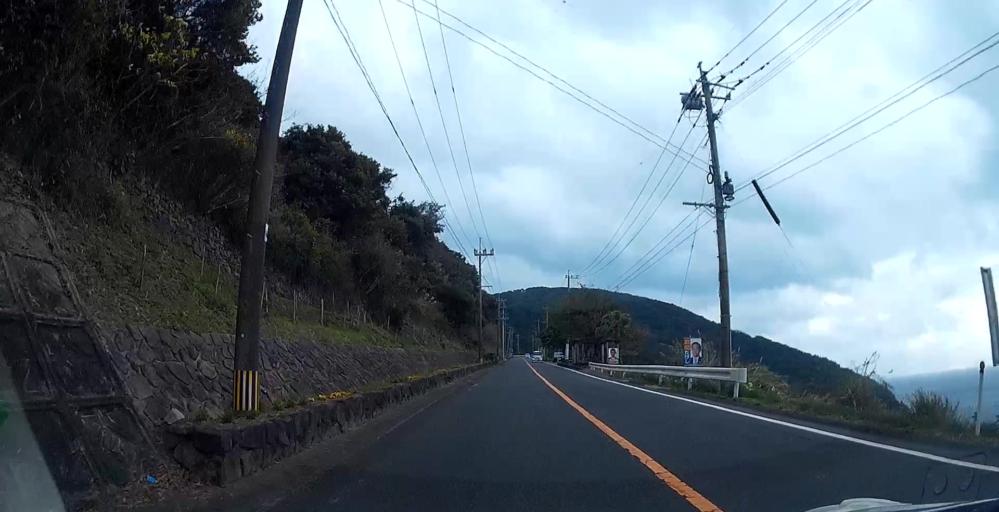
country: JP
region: Kagoshima
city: Akune
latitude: 32.1015
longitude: 130.1522
